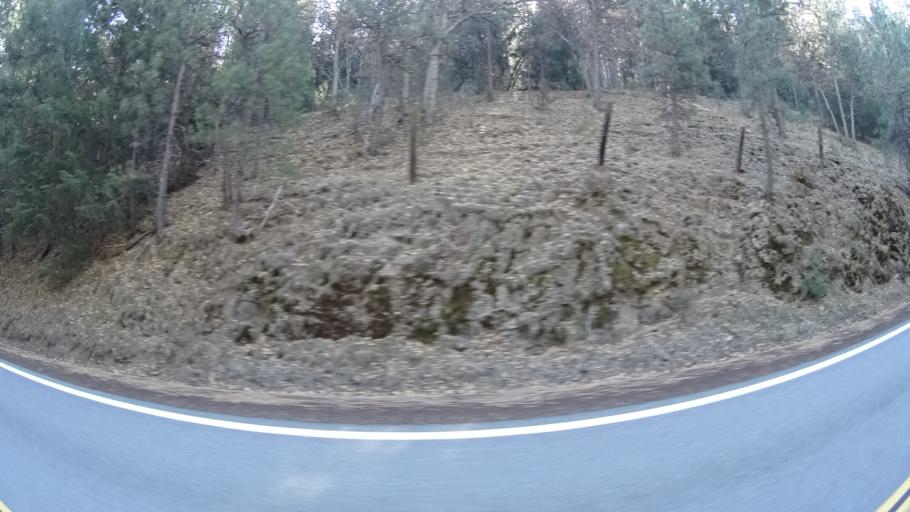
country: US
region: California
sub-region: Siskiyou County
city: Weed
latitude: 41.4661
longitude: -122.6034
